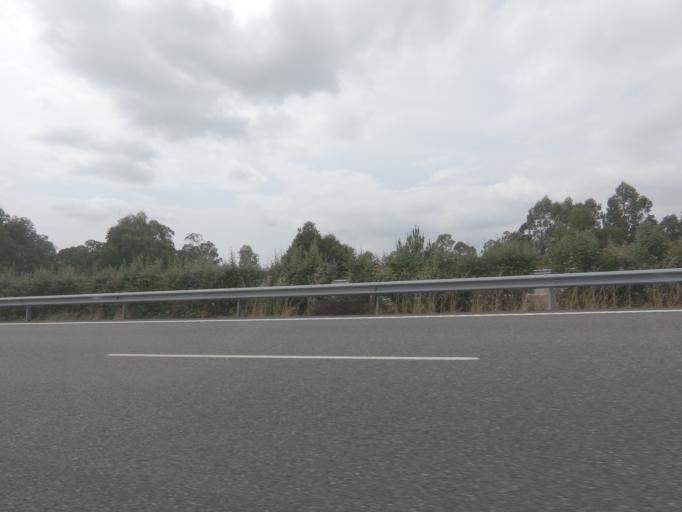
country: ES
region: Galicia
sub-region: Provincia de Pontevedra
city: Ponteareas
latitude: 42.1454
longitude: -8.4494
